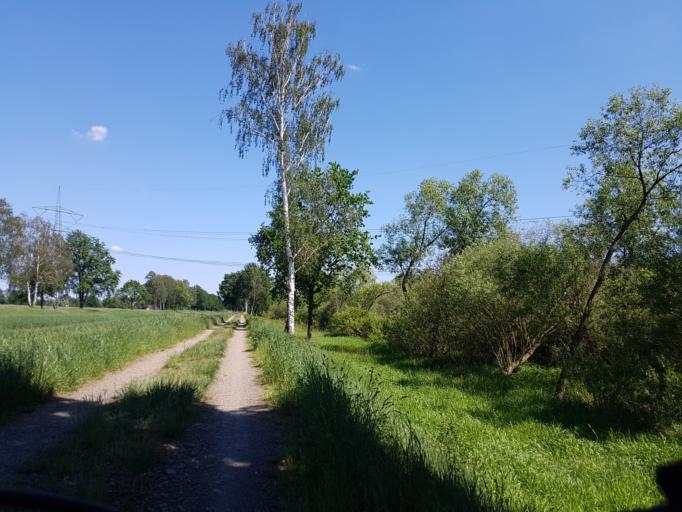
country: DE
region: Brandenburg
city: Merzdorf
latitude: 51.4301
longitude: 13.5486
